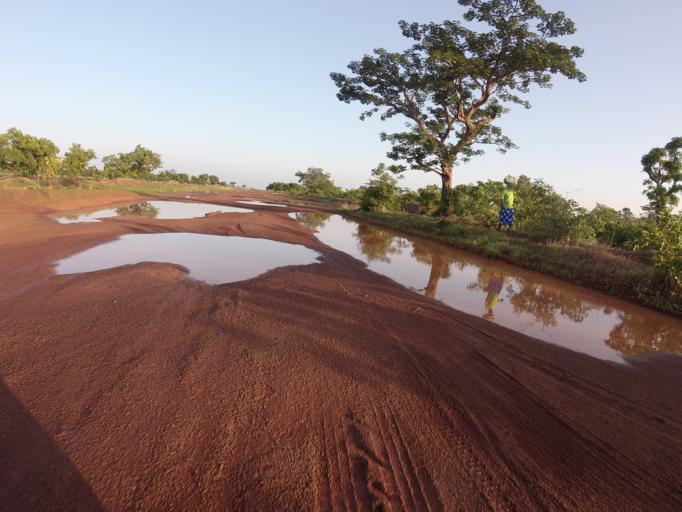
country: TG
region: Savanes
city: Sansanne-Mango
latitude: 10.2335
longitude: -0.0733
